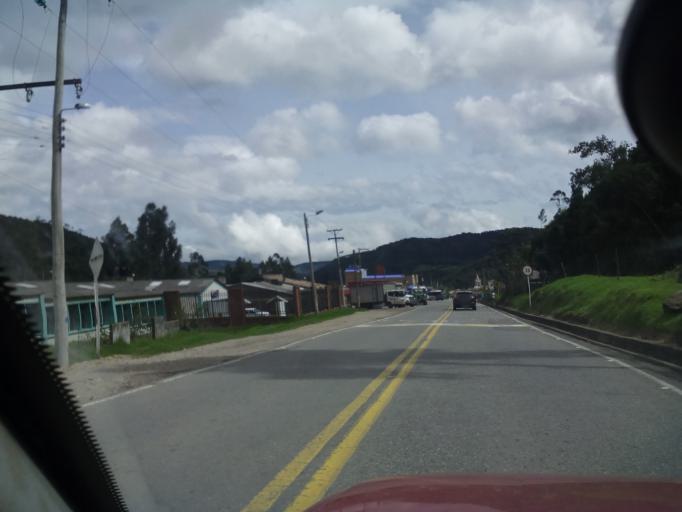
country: CO
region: Boyaca
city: Arcabuco
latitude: 5.7489
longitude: -73.4331
